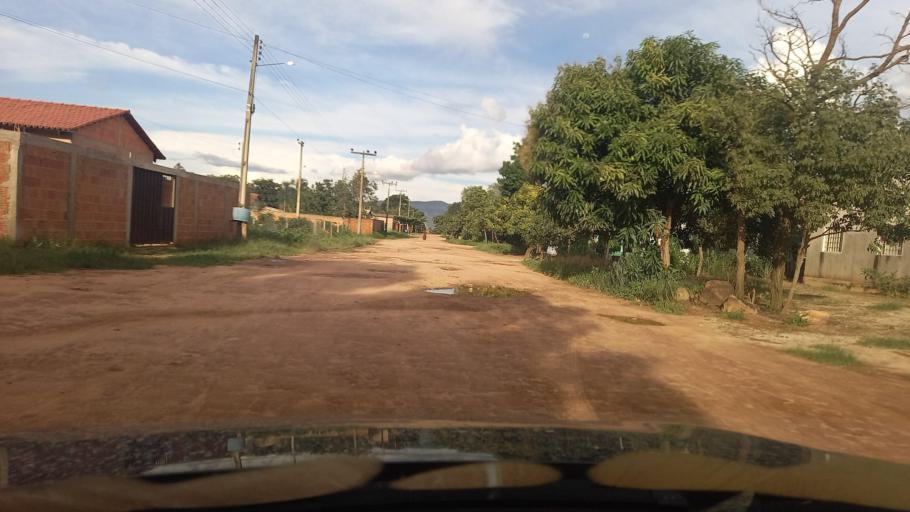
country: BR
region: Goias
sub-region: Cavalcante
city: Cavalcante
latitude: -13.7998
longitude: -47.4431
